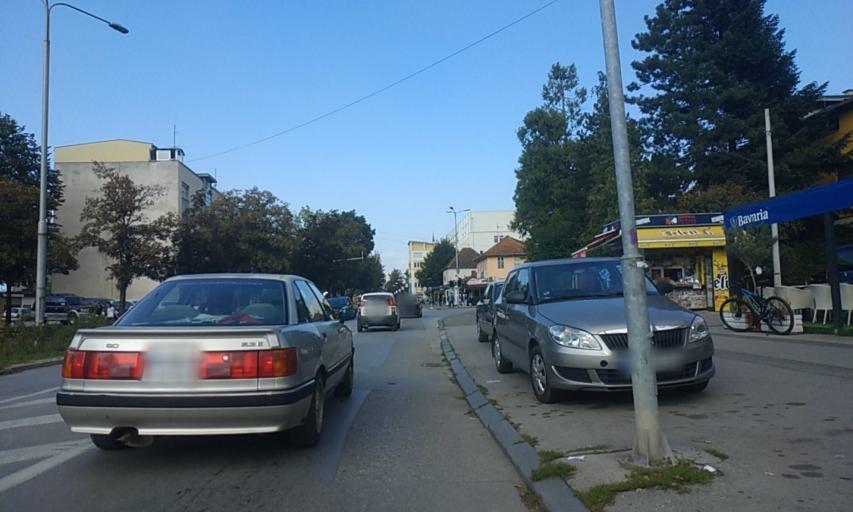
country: BA
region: Republika Srpska
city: Hiseti
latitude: 44.7648
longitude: 17.1842
